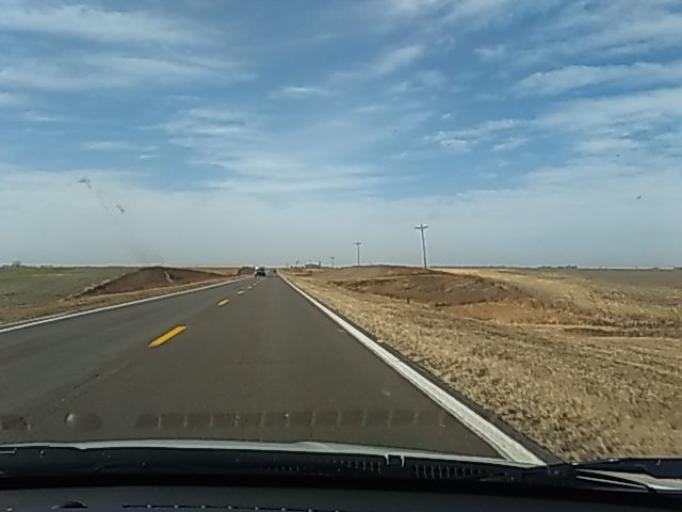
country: US
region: Nebraska
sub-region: Clay County
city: Clay Center
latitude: 40.4233
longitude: -97.9998
